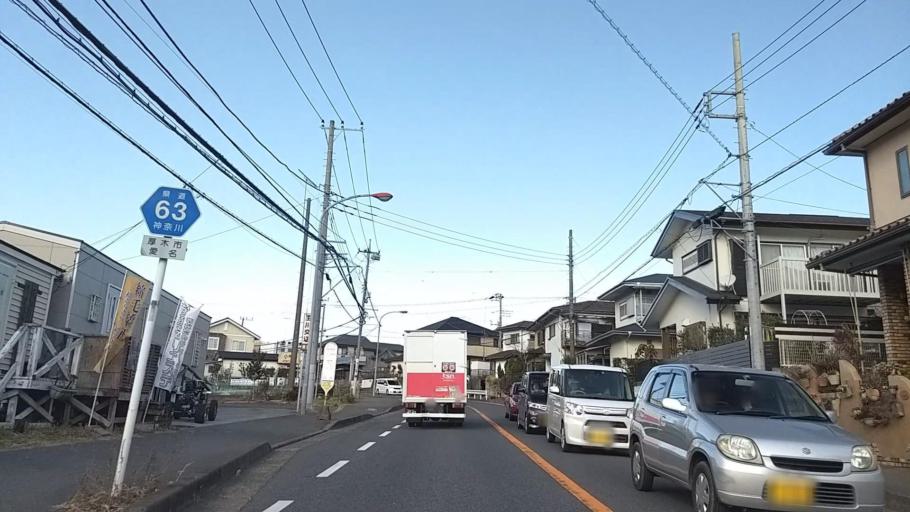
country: JP
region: Kanagawa
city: Atsugi
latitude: 35.4358
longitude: 139.3246
